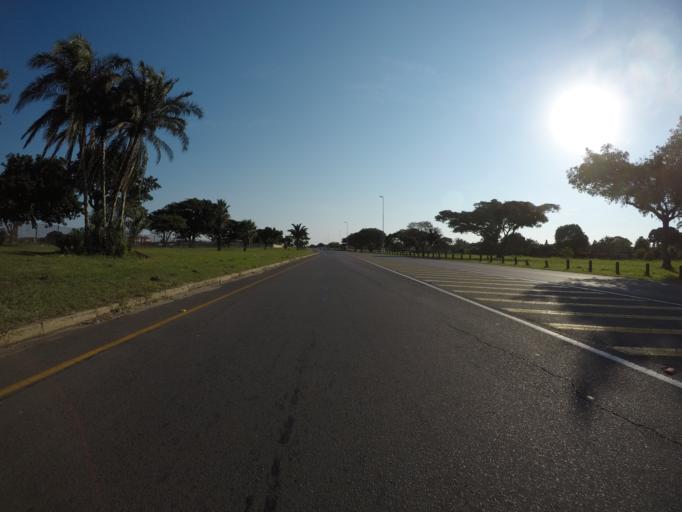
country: ZA
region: KwaZulu-Natal
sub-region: uThungulu District Municipality
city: Richards Bay
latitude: -28.7602
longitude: 32.0588
